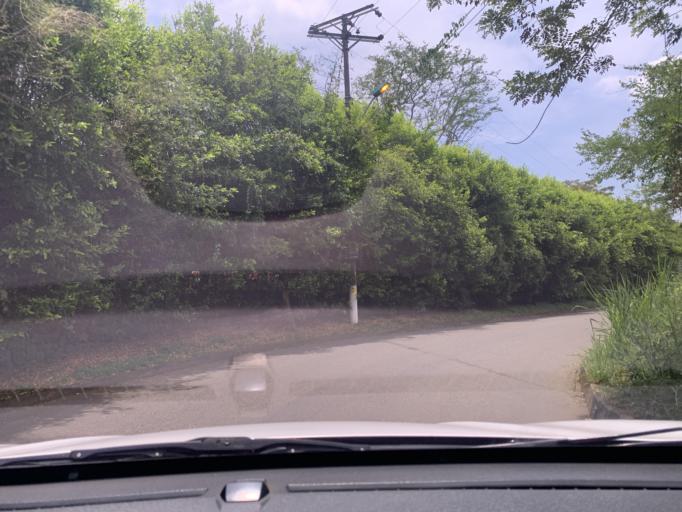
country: CO
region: Valle del Cauca
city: Jamundi
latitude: 3.3366
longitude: -76.5511
